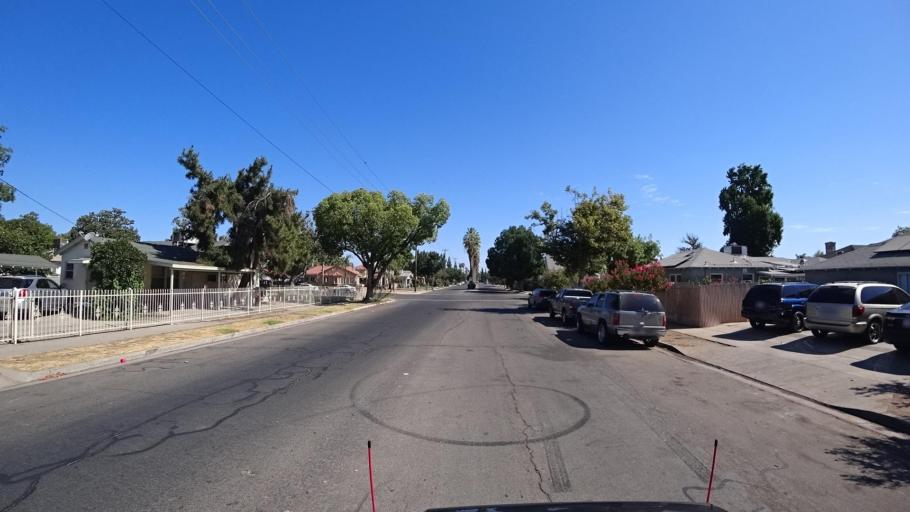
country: US
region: California
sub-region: Fresno County
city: Fresno
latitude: 36.7323
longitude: -119.7659
